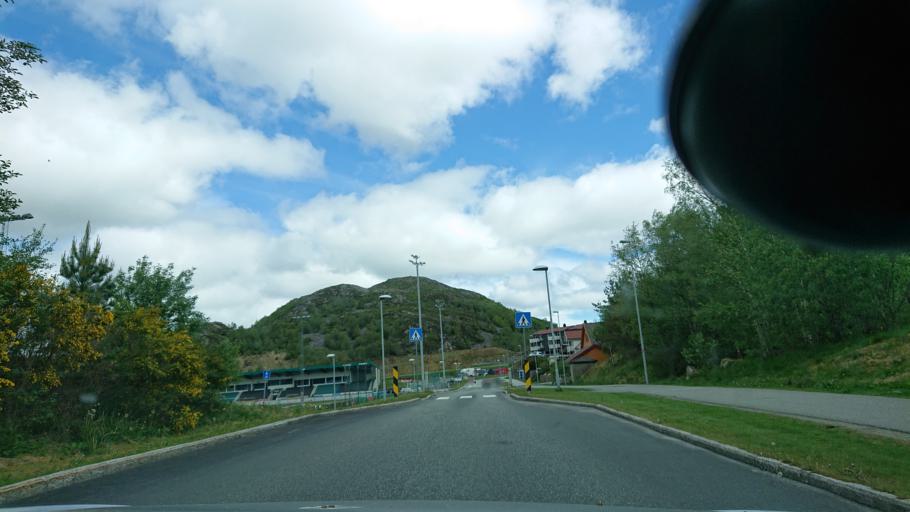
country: NO
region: Rogaland
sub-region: Gjesdal
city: Algard
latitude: 58.7736
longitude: 5.8663
